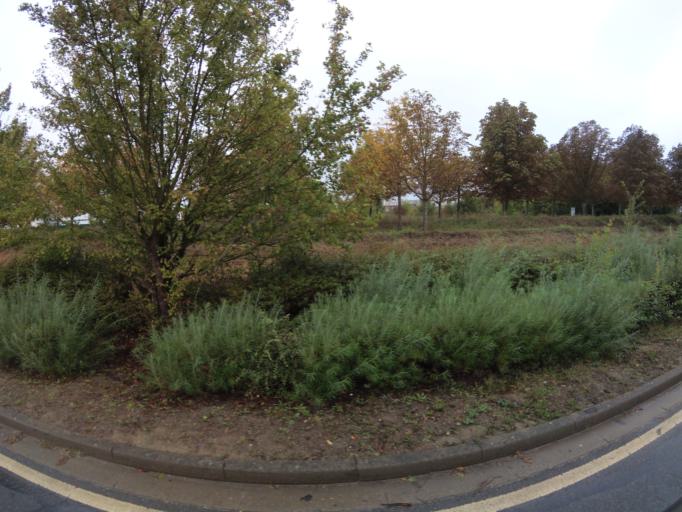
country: FR
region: Ile-de-France
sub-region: Departement de Seine-et-Marne
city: Chanteloup-en-Brie
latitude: 48.8339
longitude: 2.7332
